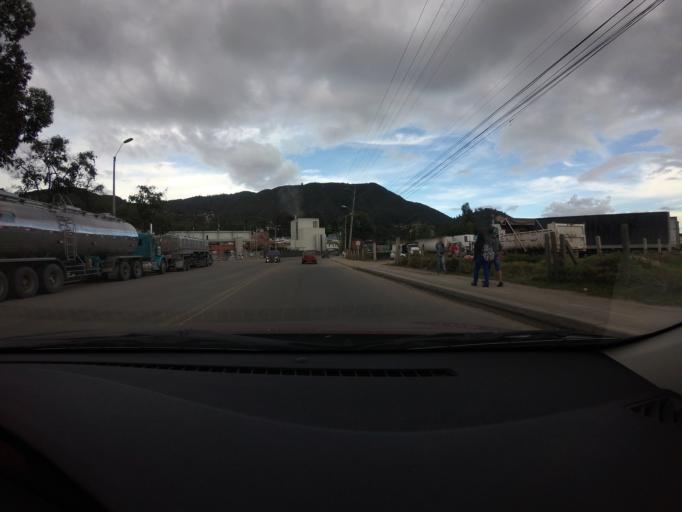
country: CO
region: Cundinamarca
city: Sopo
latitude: 4.9156
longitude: -73.9439
